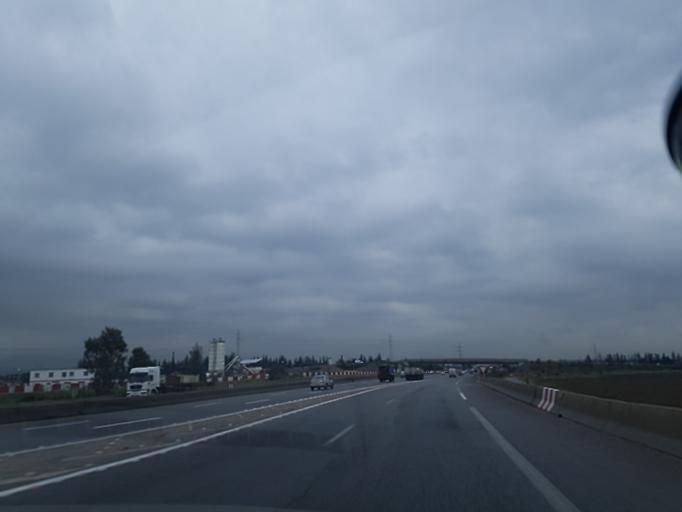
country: DZ
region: Boumerdes
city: Khemis el Khechna
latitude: 36.6657
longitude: 3.3289
